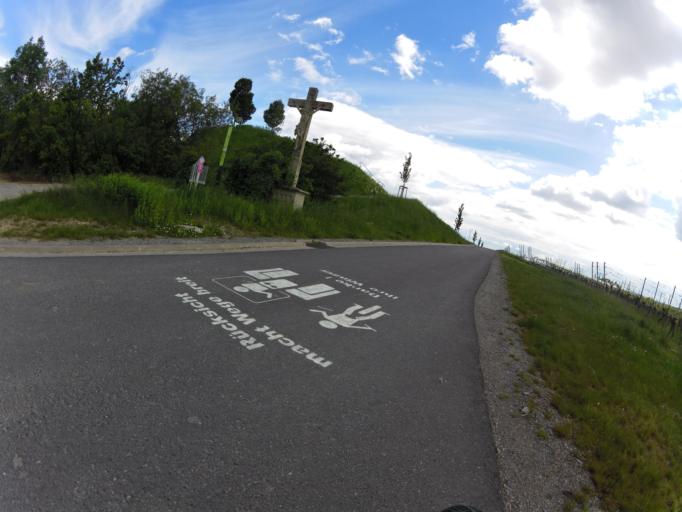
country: DE
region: Bavaria
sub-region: Regierungsbezirk Unterfranken
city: Sommerach
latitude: 49.8457
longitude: 10.1943
